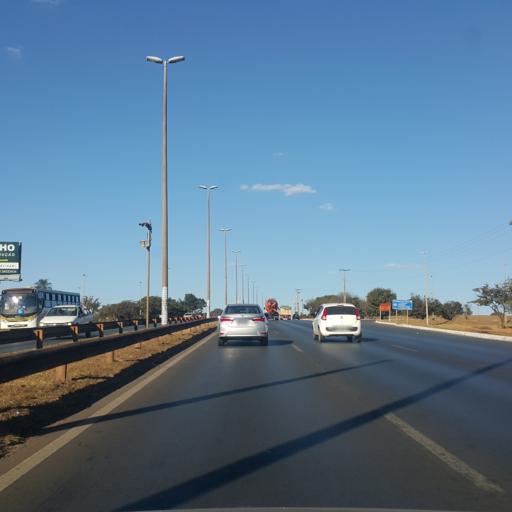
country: BR
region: Federal District
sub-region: Brasilia
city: Brasilia
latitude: -15.7862
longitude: -48.0004
